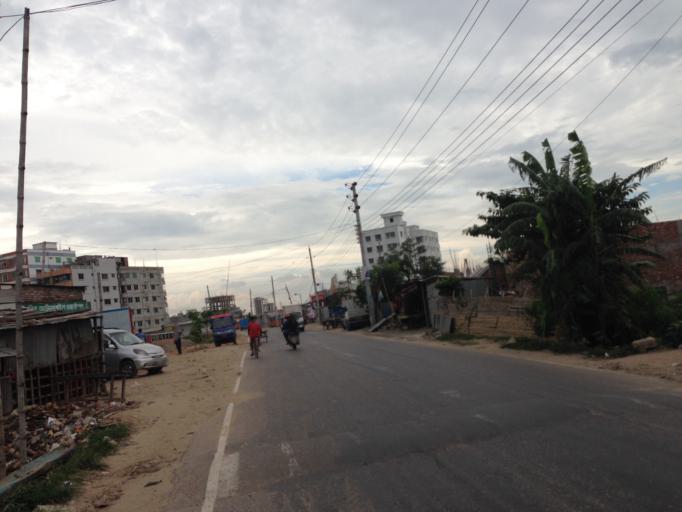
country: BD
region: Dhaka
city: Paltan
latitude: 23.7580
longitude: 90.4474
